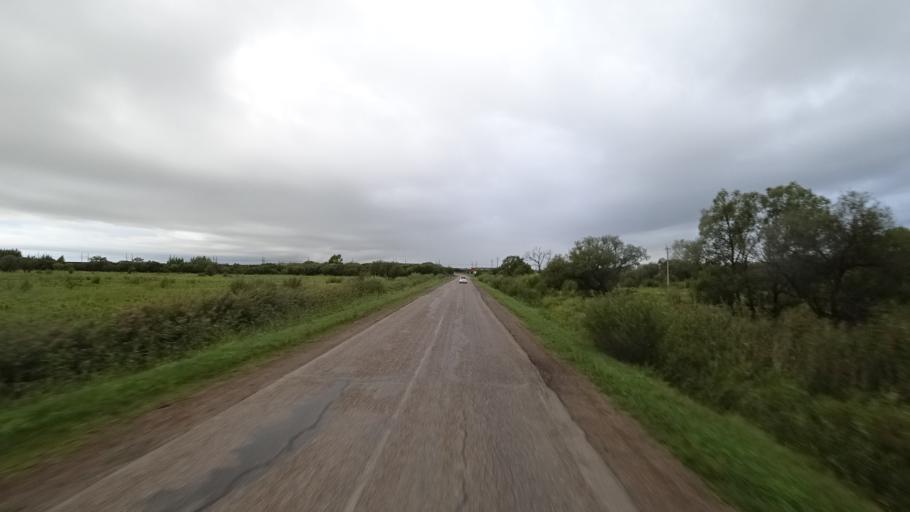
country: RU
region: Primorskiy
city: Chernigovka
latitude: 44.3614
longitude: 132.5547
